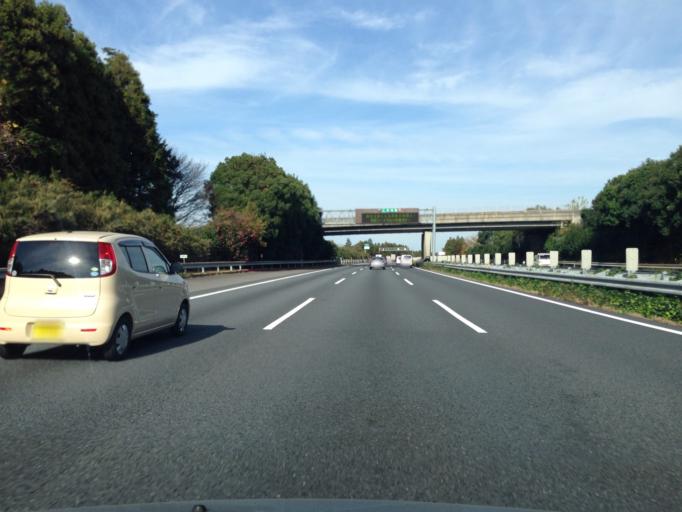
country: JP
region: Ibaraki
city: Ishioka
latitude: 36.2505
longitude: 140.2970
